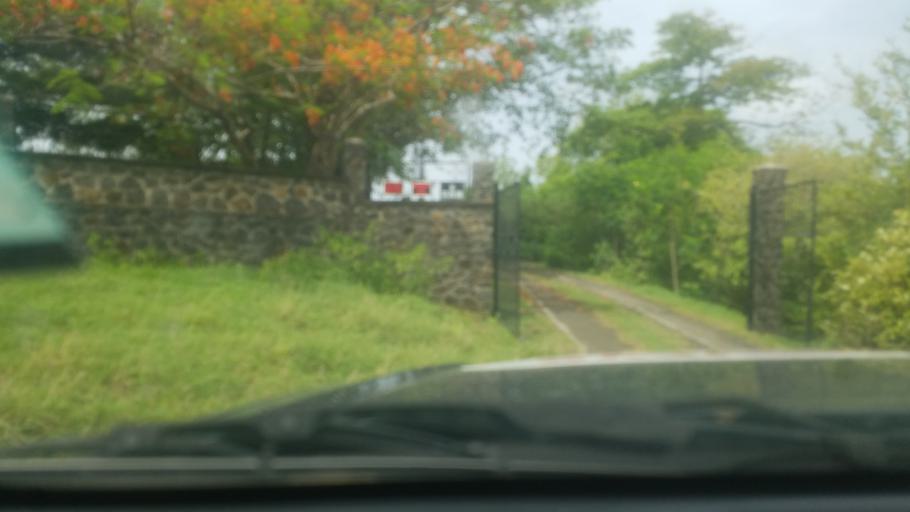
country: LC
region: Laborie Quarter
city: Laborie
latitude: 13.7513
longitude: -61.0069
